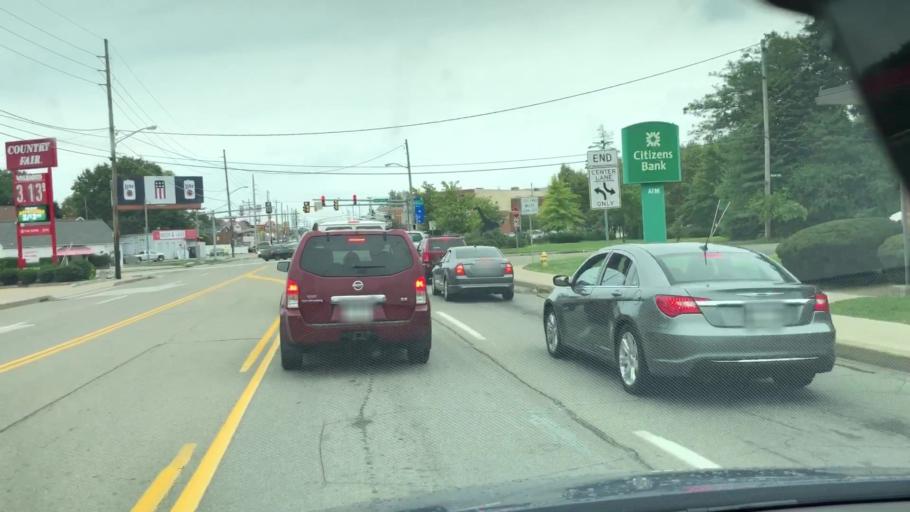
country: US
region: Pennsylvania
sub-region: Erie County
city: Erie
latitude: 42.0957
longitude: -80.0824
